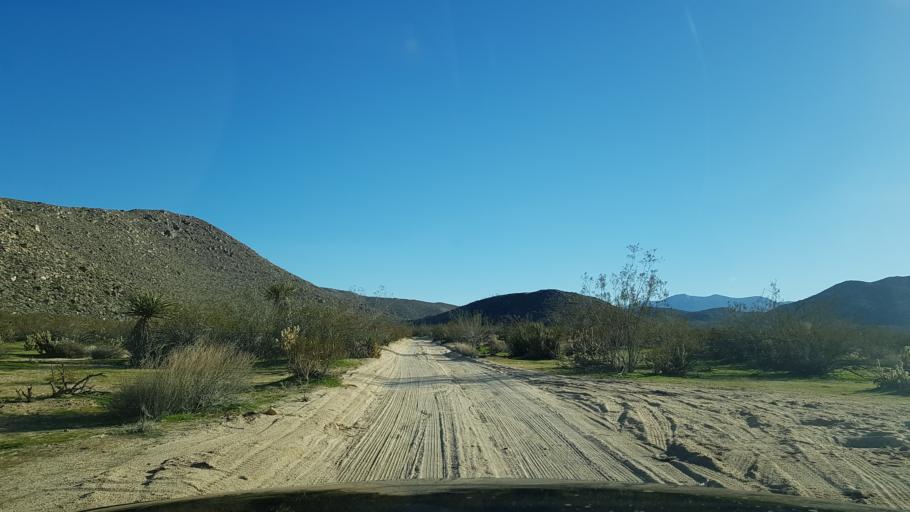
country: US
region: California
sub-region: San Diego County
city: Julian
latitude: 33.0216
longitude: -116.3952
